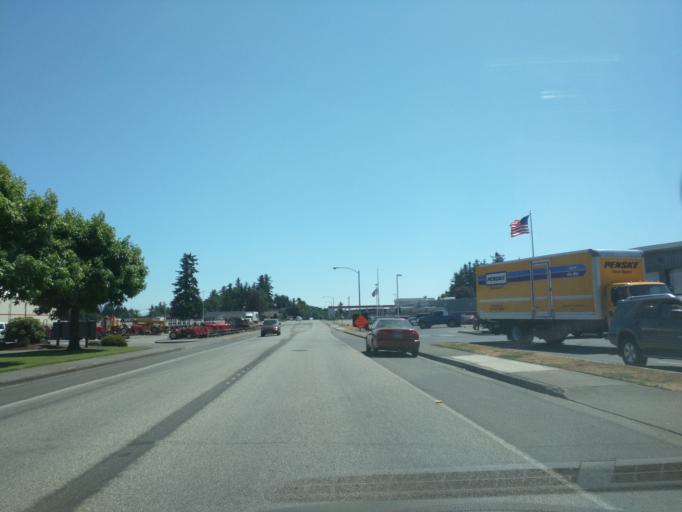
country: US
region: Washington
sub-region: Whatcom County
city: Lynden
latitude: 48.9417
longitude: -122.4810
